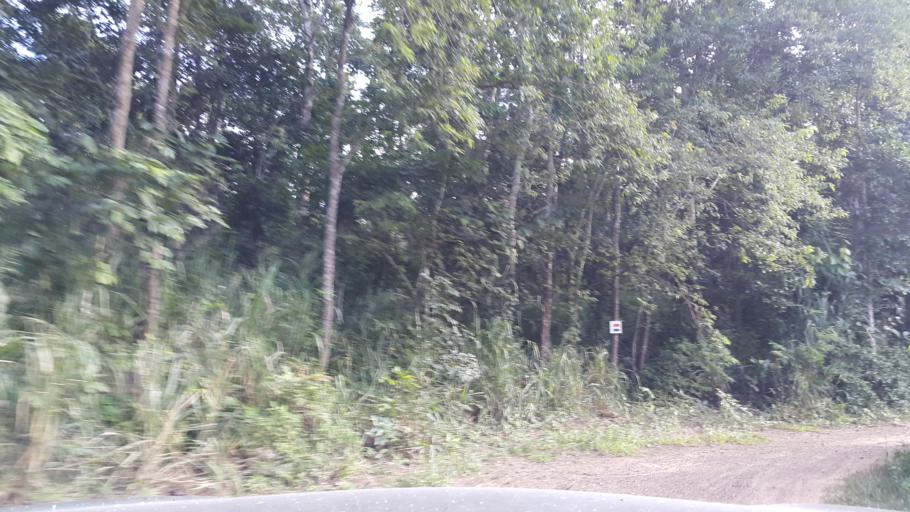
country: TH
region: Chiang Mai
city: San Sai
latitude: 18.9261
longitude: 99.0501
